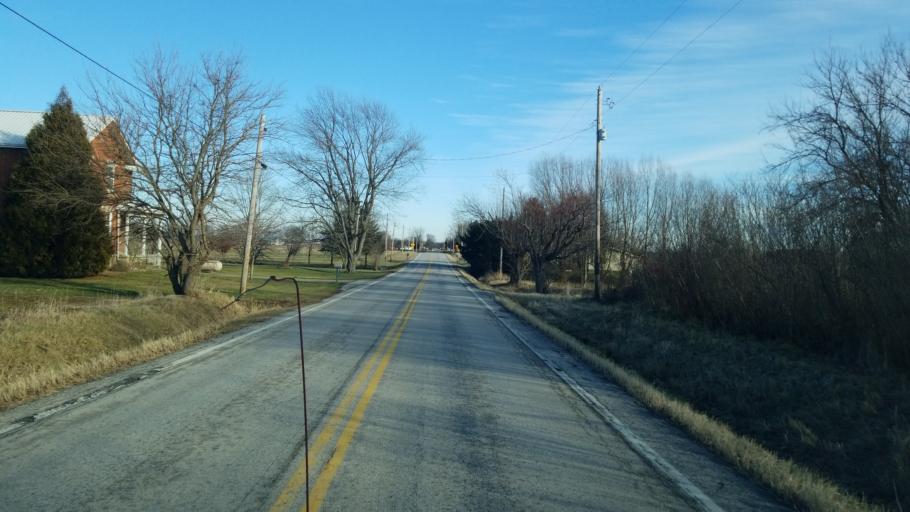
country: US
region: Ohio
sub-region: Huron County
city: Bellevue
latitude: 41.2023
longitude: -82.8294
